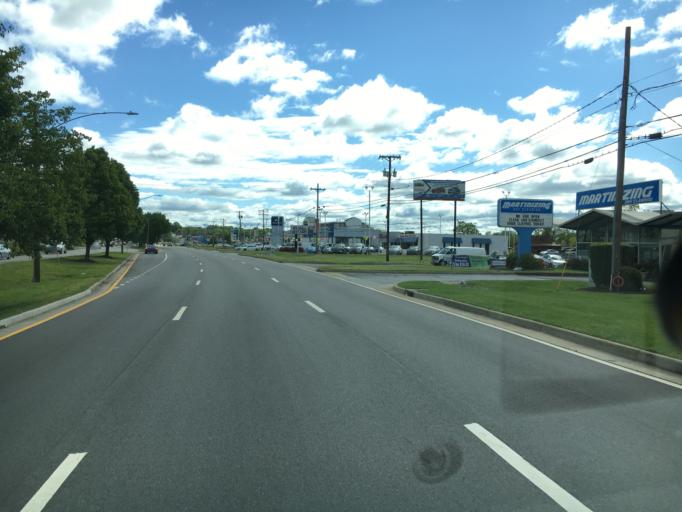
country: US
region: Virginia
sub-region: City of Danville
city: Danville
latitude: 36.5949
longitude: -79.4076
